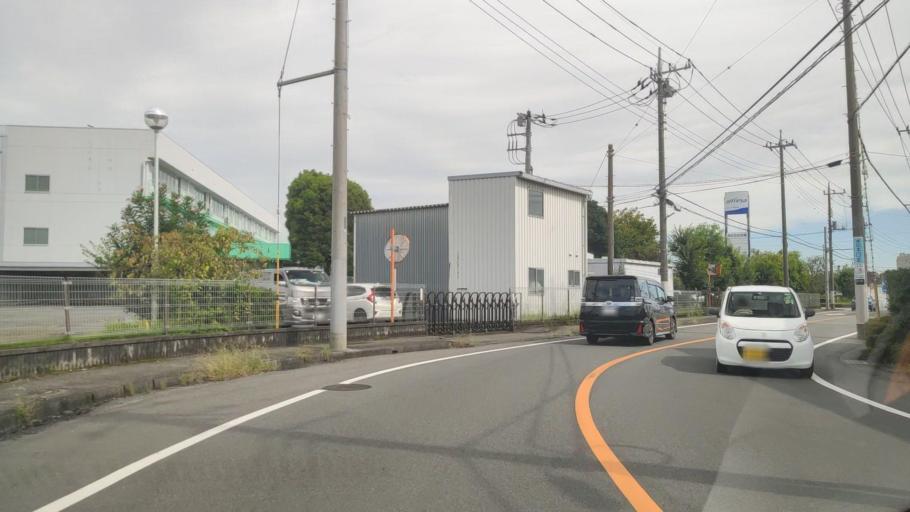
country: JP
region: Gunma
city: Takasaki
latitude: 36.3604
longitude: 139.0100
